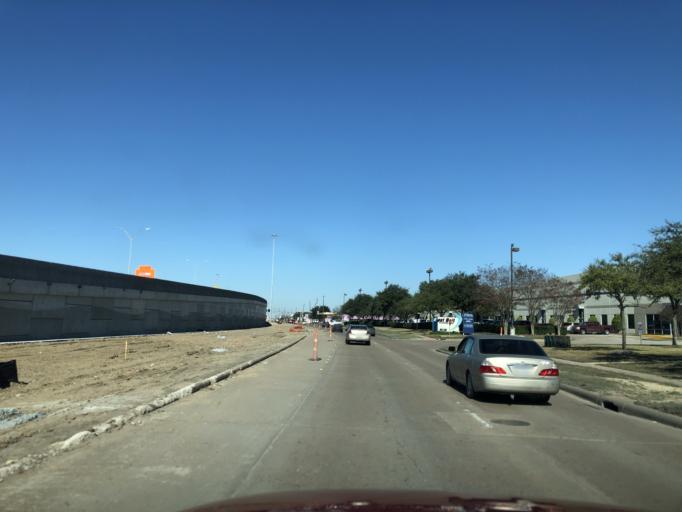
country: US
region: Texas
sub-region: Harris County
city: Deer Park
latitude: 29.6868
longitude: -95.1533
